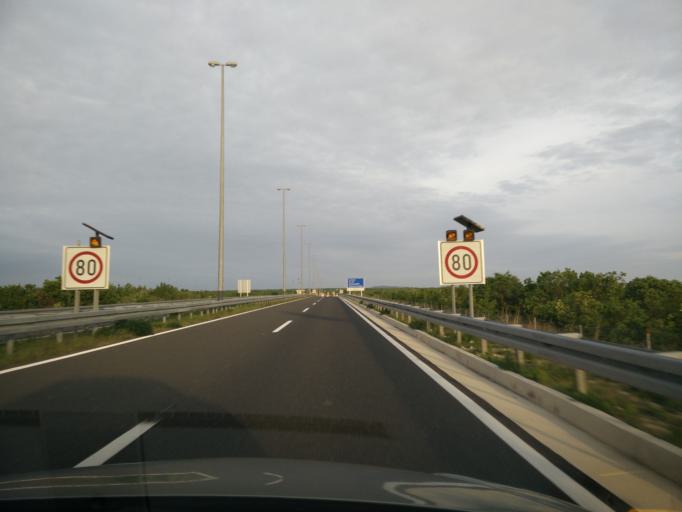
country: HR
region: Zadarska
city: Galovac
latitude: 44.1177
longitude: 15.4309
